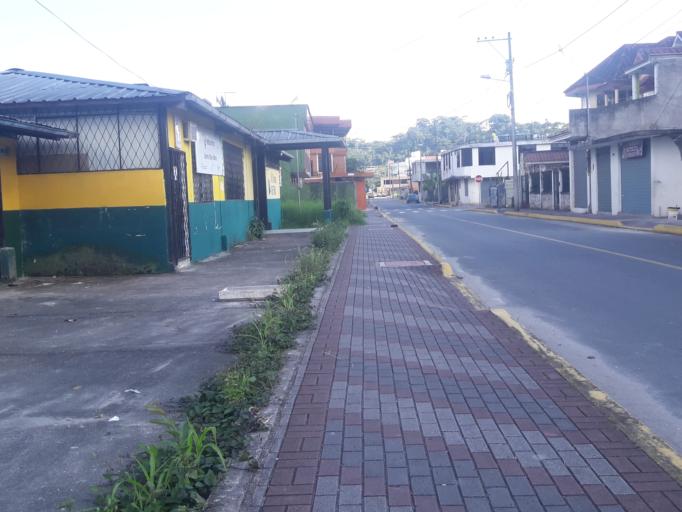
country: EC
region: Napo
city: Tena
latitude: -1.0044
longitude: -77.8136
